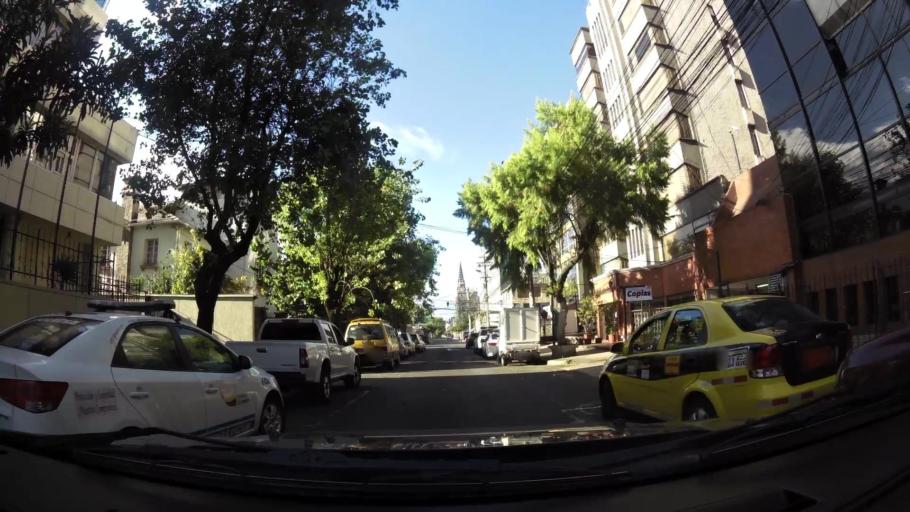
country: EC
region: Pichincha
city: Quito
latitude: -0.2070
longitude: -78.4977
